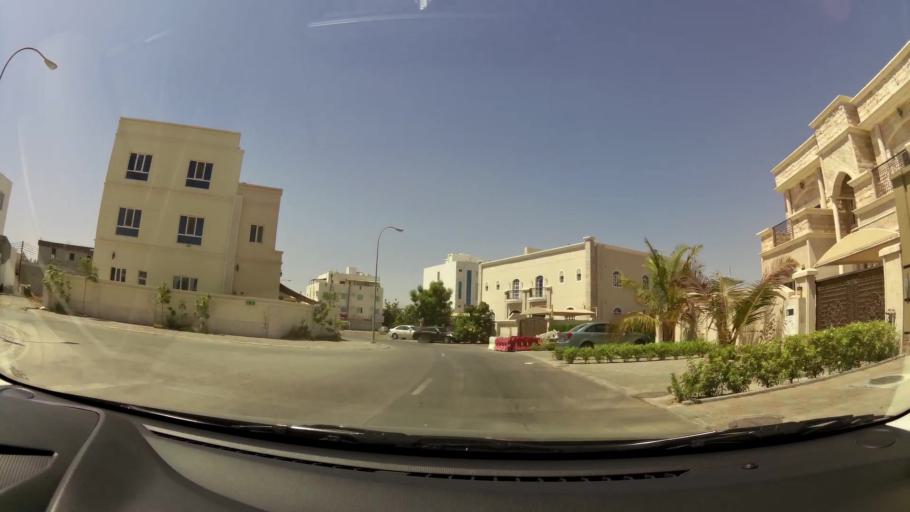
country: OM
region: Muhafazat Masqat
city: As Sib al Jadidah
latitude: 23.6259
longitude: 58.2504
